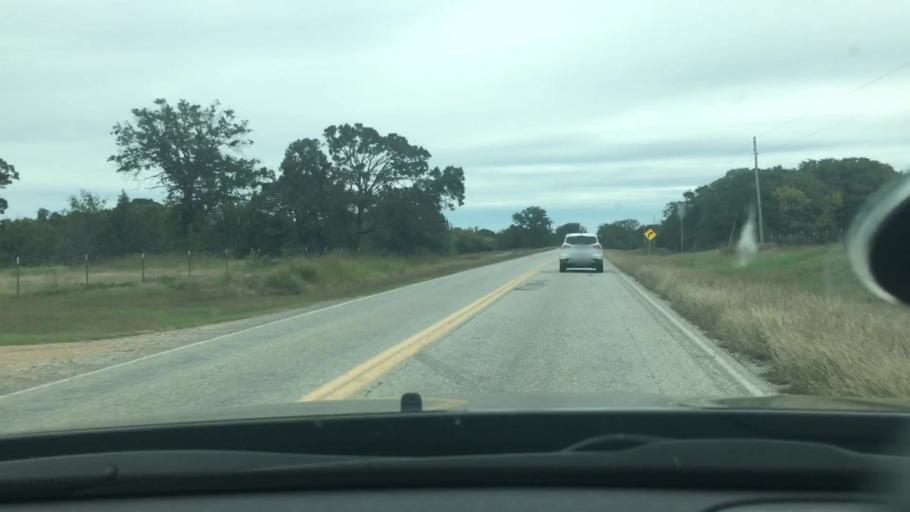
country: US
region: Oklahoma
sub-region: Johnston County
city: Tishomingo
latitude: 34.3186
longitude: -96.4247
